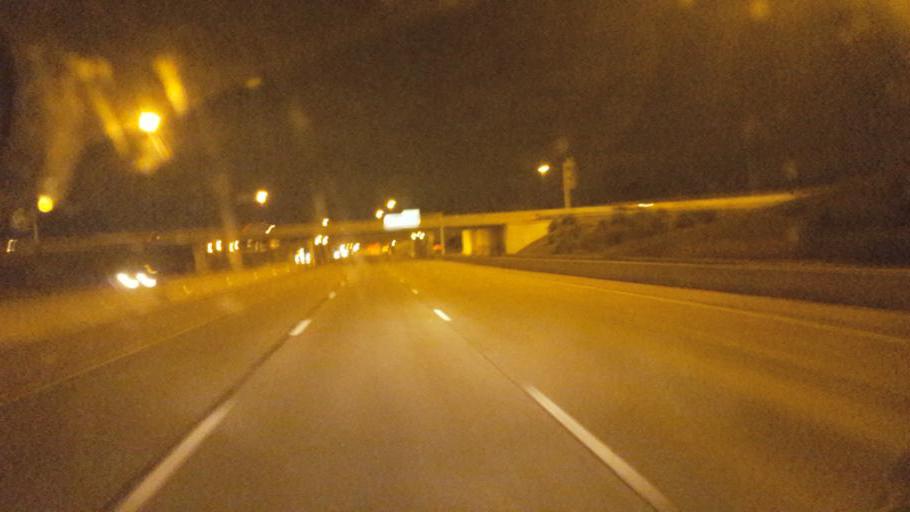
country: US
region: Indiana
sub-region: Marion County
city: Warren Park
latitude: 39.7992
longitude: -86.0328
